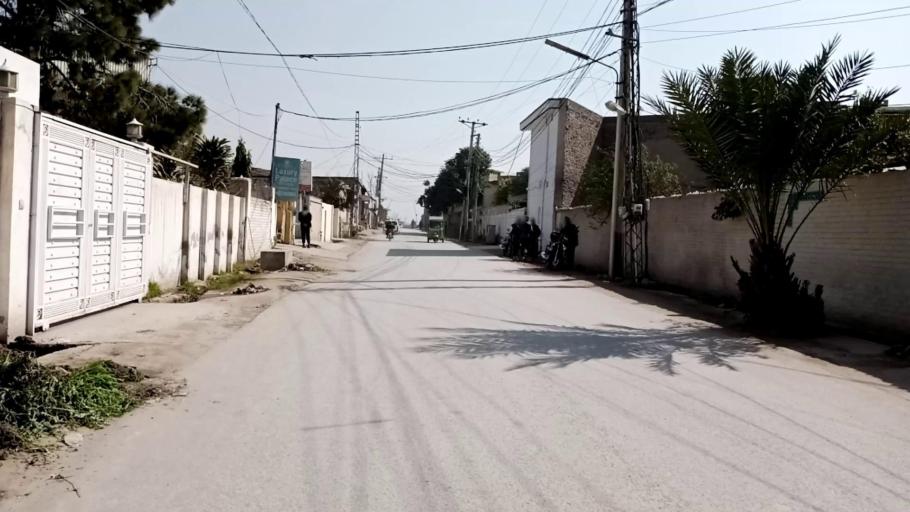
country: PK
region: Khyber Pakhtunkhwa
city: Peshawar
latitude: 33.9948
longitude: 71.5069
